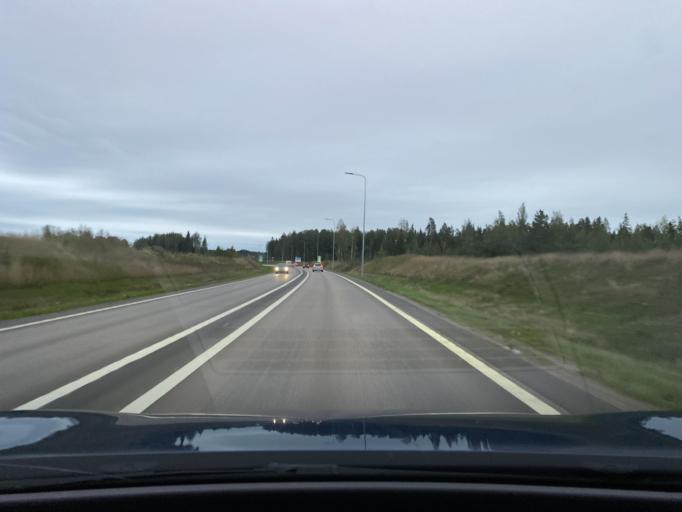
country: FI
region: Paijanne Tavastia
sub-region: Lahti
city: Lahti
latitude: 60.9528
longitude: 25.5783
